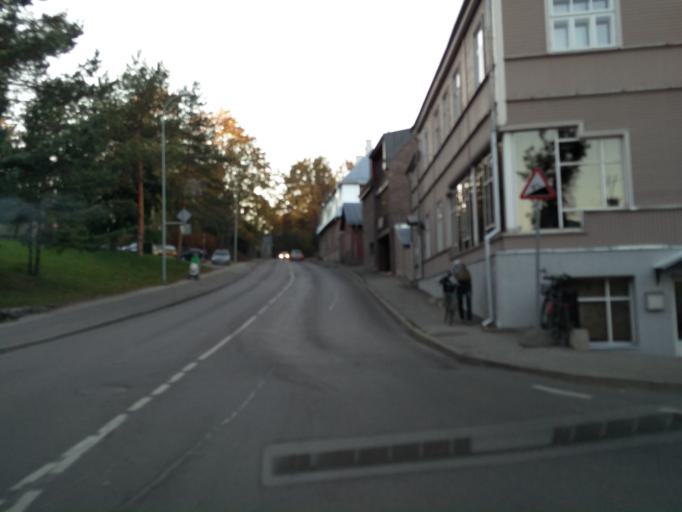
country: EE
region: Tartu
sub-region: Tartu linn
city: Tartu
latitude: 58.3824
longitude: 26.7145
